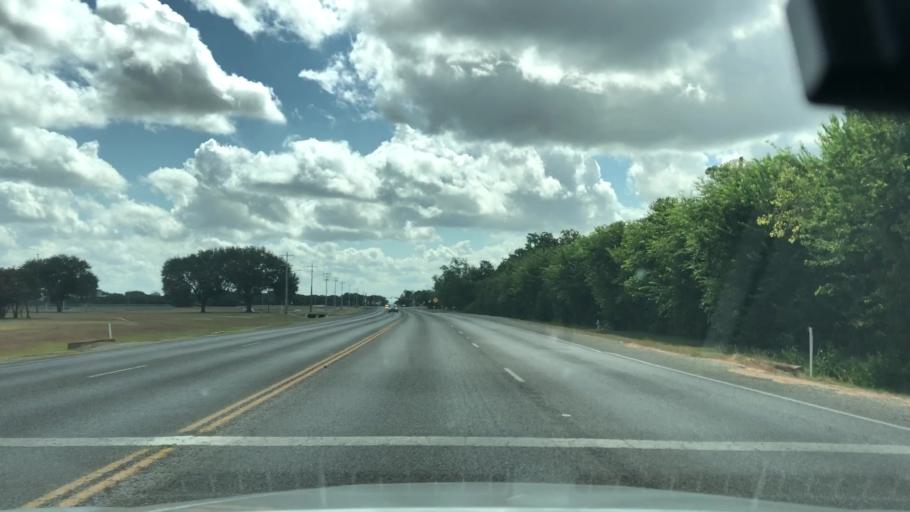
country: US
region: Texas
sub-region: Guadalupe County
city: Seguin
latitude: 29.5693
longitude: -97.9948
